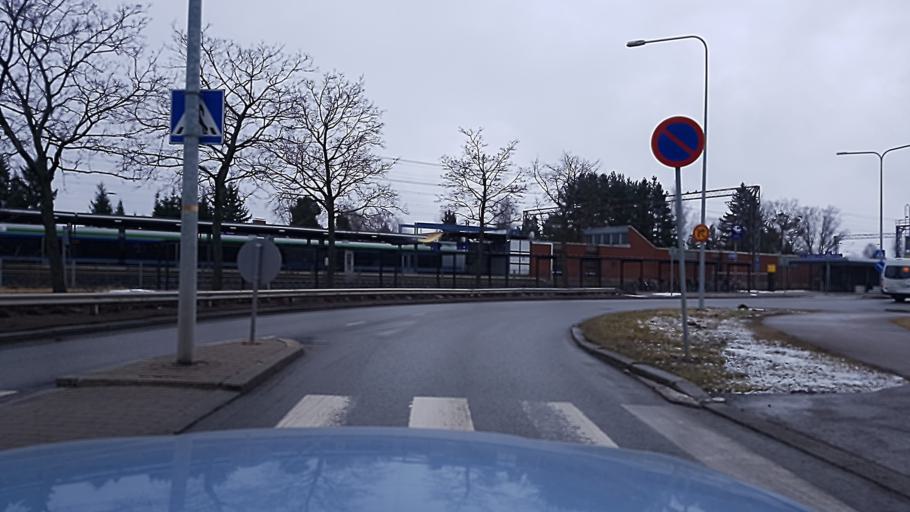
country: FI
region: Uusimaa
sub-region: Helsinki
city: Vantaa
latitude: 60.2756
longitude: 25.0355
